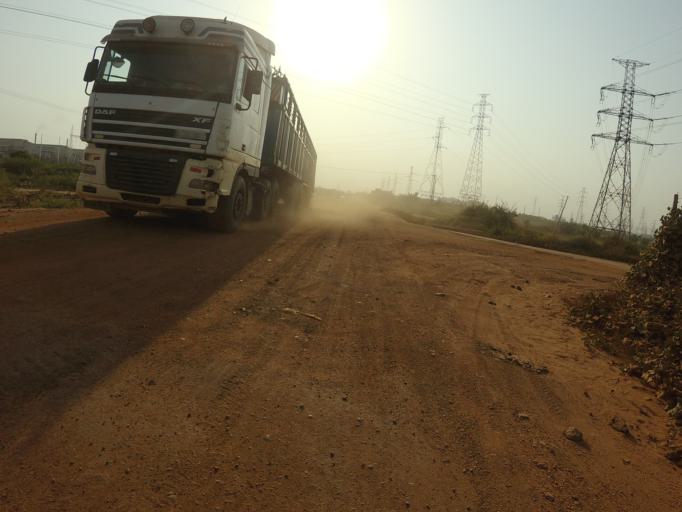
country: GH
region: Greater Accra
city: Tema
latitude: 5.6724
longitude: 0.0234
